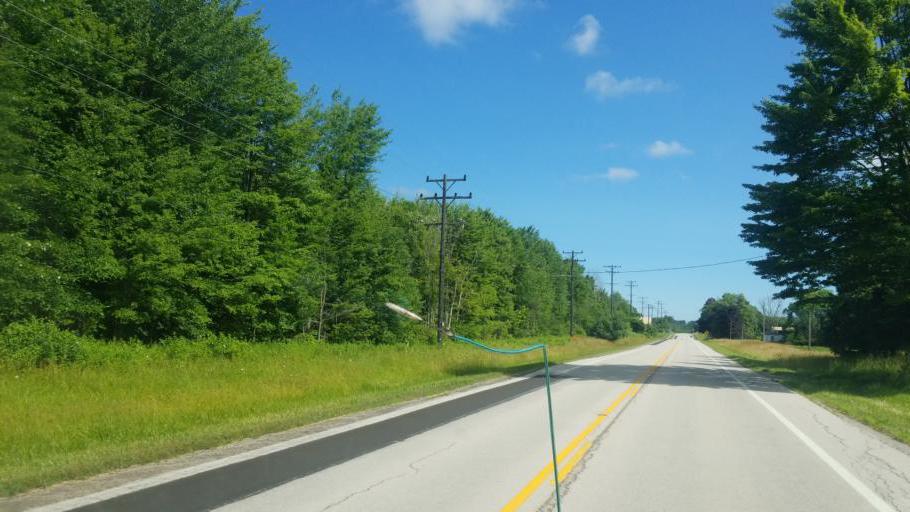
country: US
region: Ohio
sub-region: Ashtabula County
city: Conneaut
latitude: 41.8787
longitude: -80.5722
